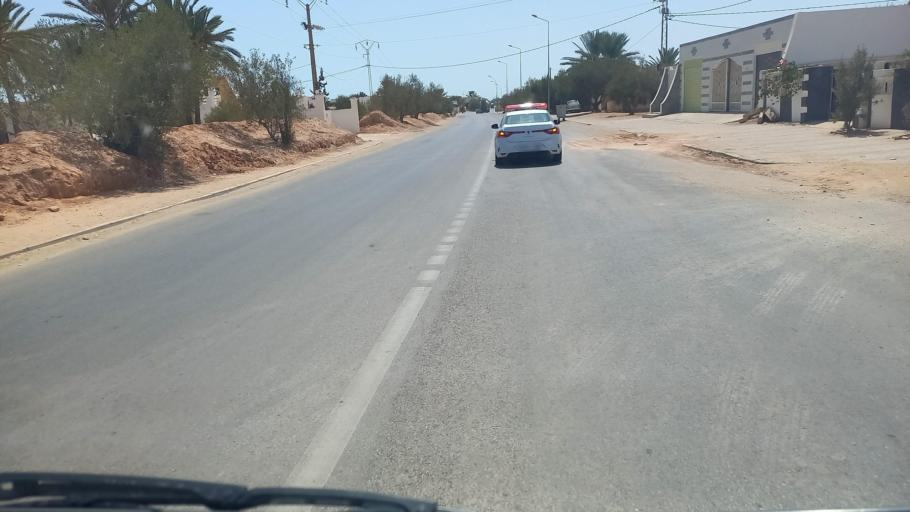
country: TN
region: Madanin
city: Midoun
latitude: 33.7711
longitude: 10.8990
